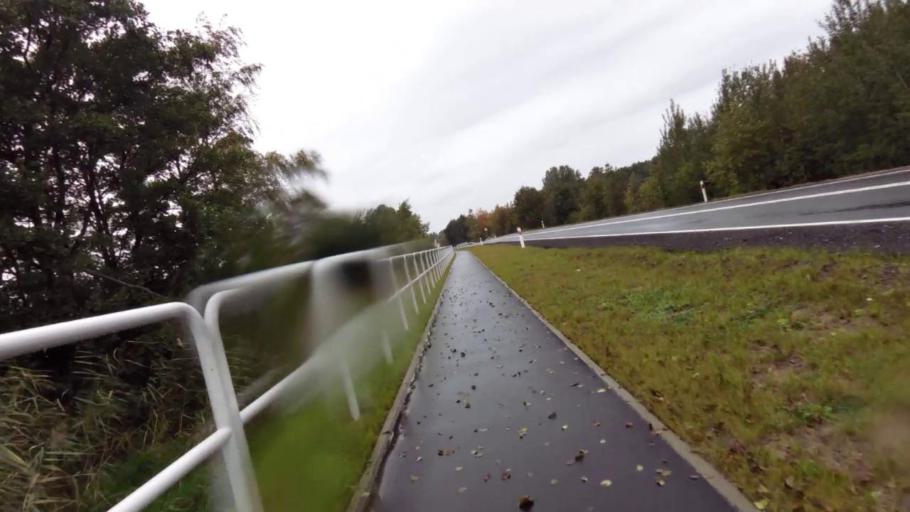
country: PL
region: West Pomeranian Voivodeship
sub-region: Powiat slawienski
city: Darlowo
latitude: 54.3737
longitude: 16.3214
